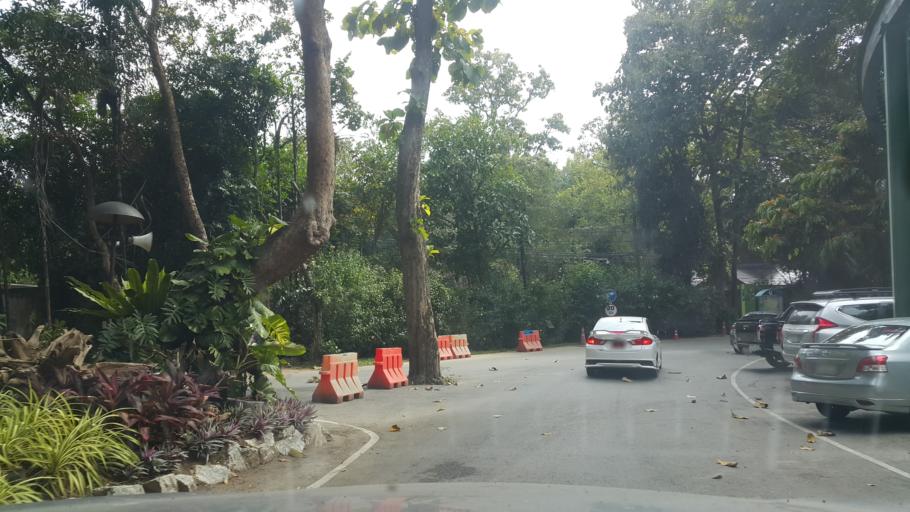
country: TH
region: Chiang Mai
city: Chiang Mai
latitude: 18.8077
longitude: 98.9471
